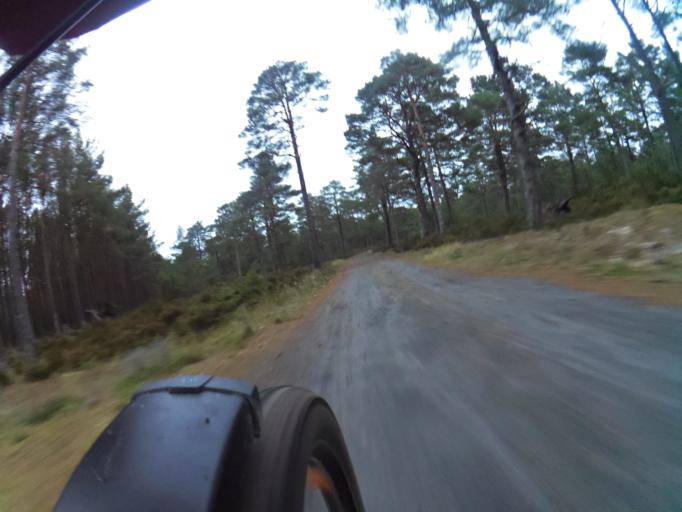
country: PL
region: Pomeranian Voivodeship
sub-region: Powiat wejherowski
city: Choczewo
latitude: 54.7981
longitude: 17.7794
